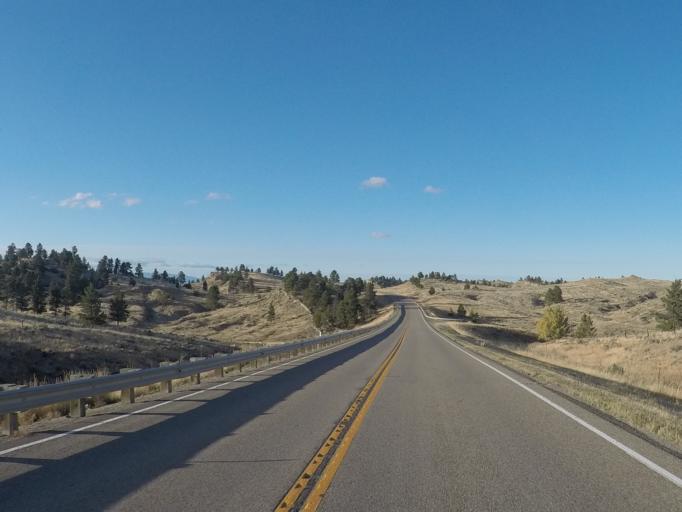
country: US
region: Montana
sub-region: Golden Valley County
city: Ryegate
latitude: 46.2608
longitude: -108.9372
